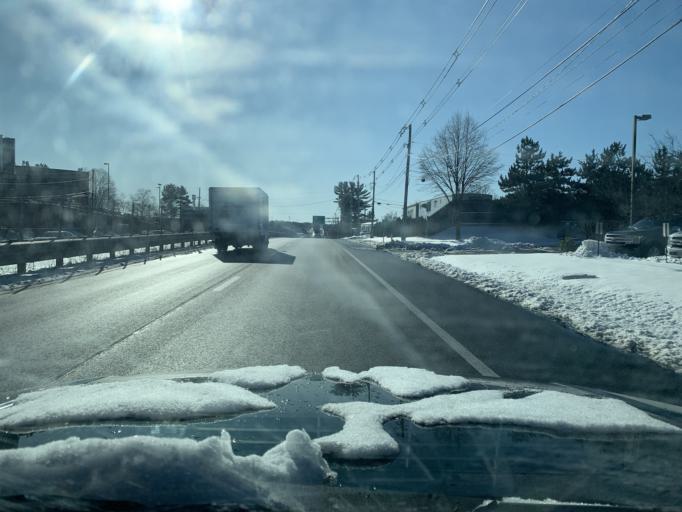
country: US
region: Massachusetts
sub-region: Essex County
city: Danvers
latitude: 42.5662
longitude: -70.9752
